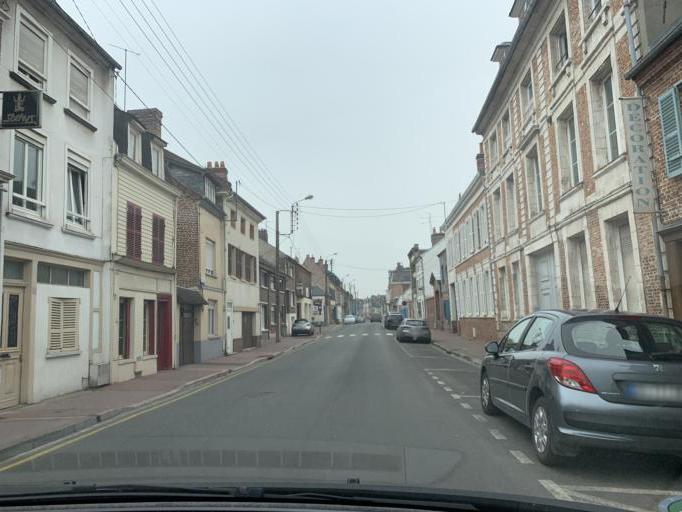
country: FR
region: Picardie
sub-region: Departement de la Somme
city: Abbeville
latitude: 50.1105
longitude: 1.8296
